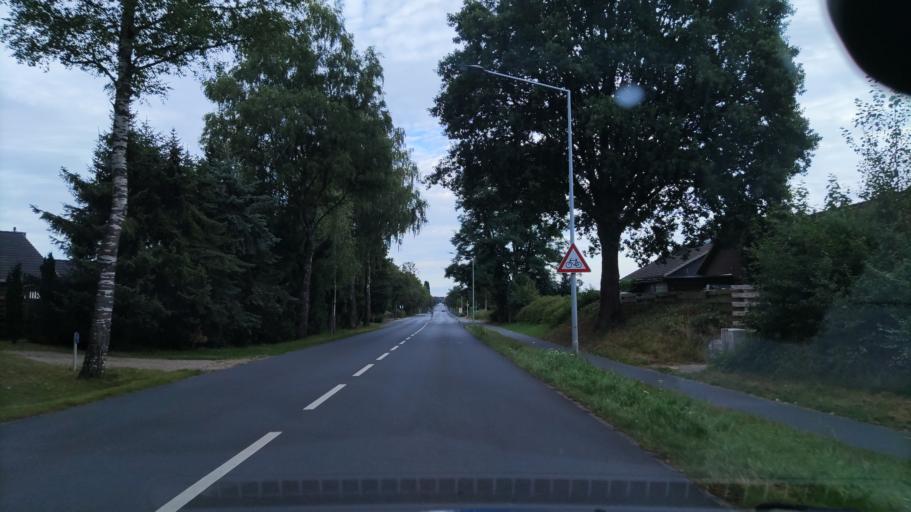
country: DE
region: Lower Saxony
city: Soltau
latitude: 52.9767
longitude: 9.8220
